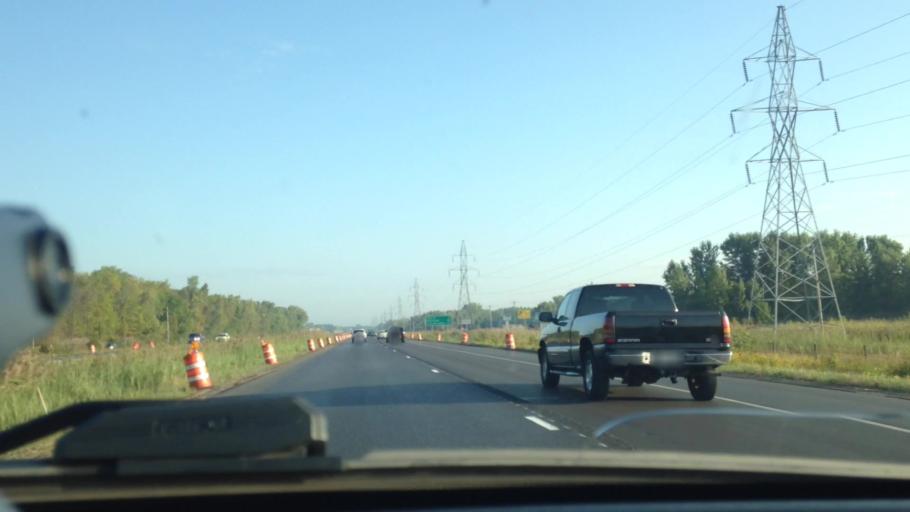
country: US
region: Wisconsin
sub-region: Brown County
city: Suamico
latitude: 44.6039
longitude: -88.0501
